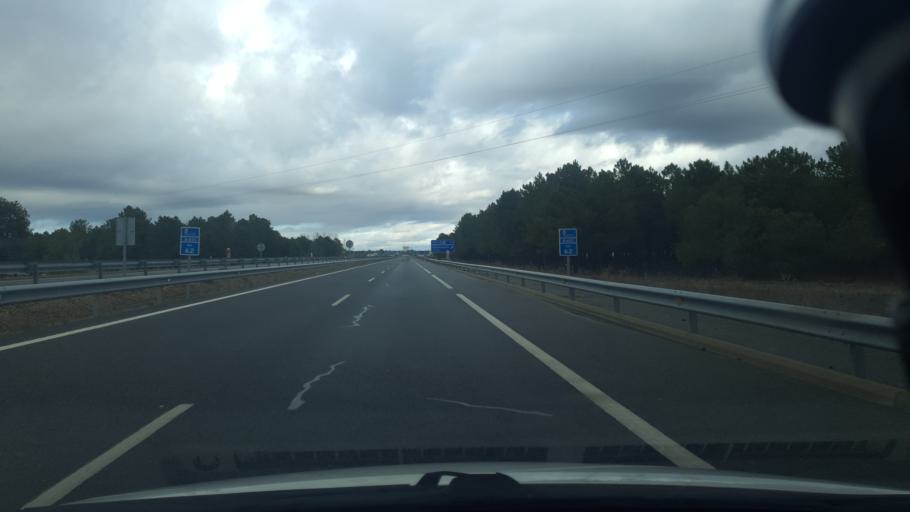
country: ES
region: Castille and Leon
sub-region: Provincia de Segovia
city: Sanchonuno
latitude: 41.3338
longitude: -4.3091
